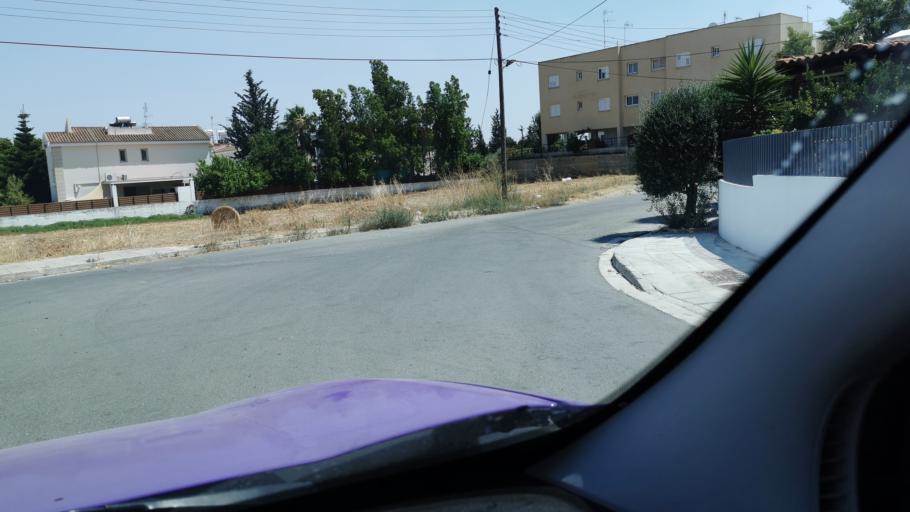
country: CY
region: Lefkosia
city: Kato Deftera
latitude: 35.1227
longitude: 33.3001
